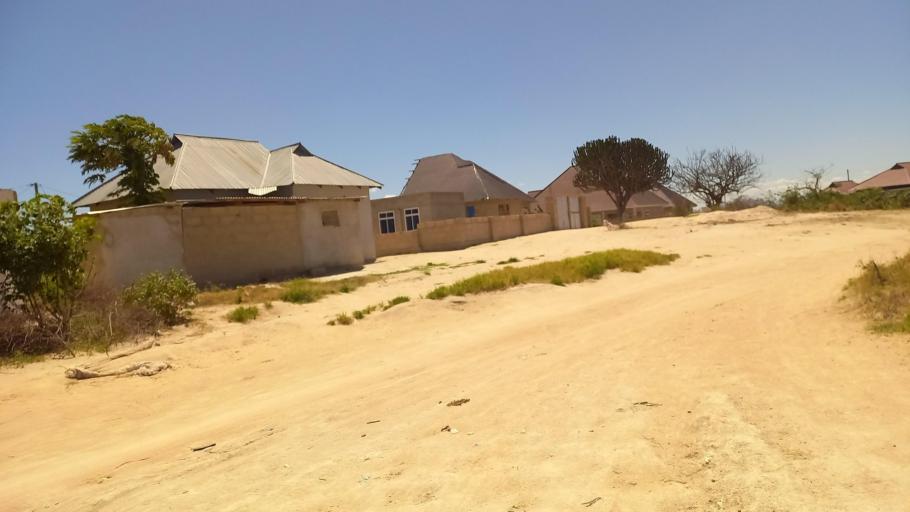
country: TZ
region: Dodoma
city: Dodoma
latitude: -6.1352
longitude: 35.7105
